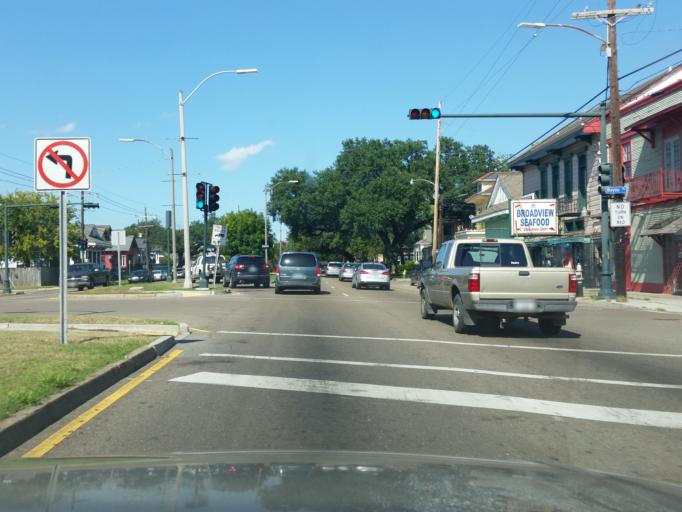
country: US
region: Louisiana
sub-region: Orleans Parish
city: New Orleans
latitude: 29.9772
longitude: -90.0770
